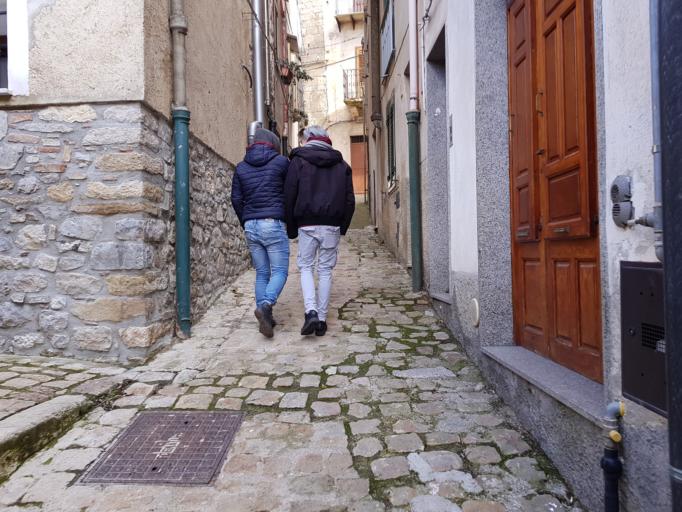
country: IT
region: Sicily
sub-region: Palermo
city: Polizzi Generosa
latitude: 37.8116
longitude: 14.0024
